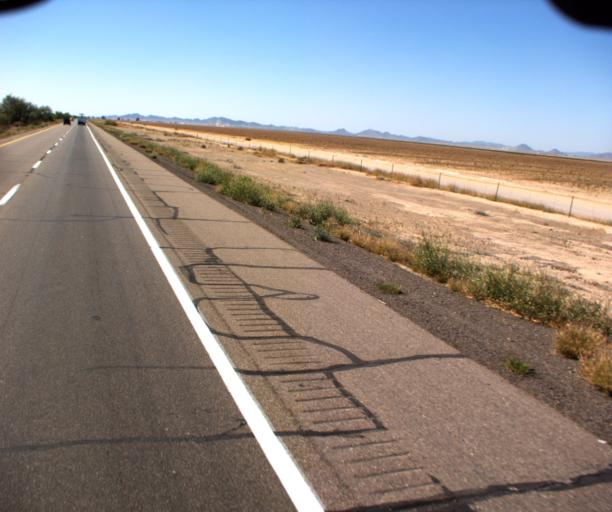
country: US
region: Arizona
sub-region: Maricopa County
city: Gila Bend
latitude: 32.9271
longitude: -112.8492
